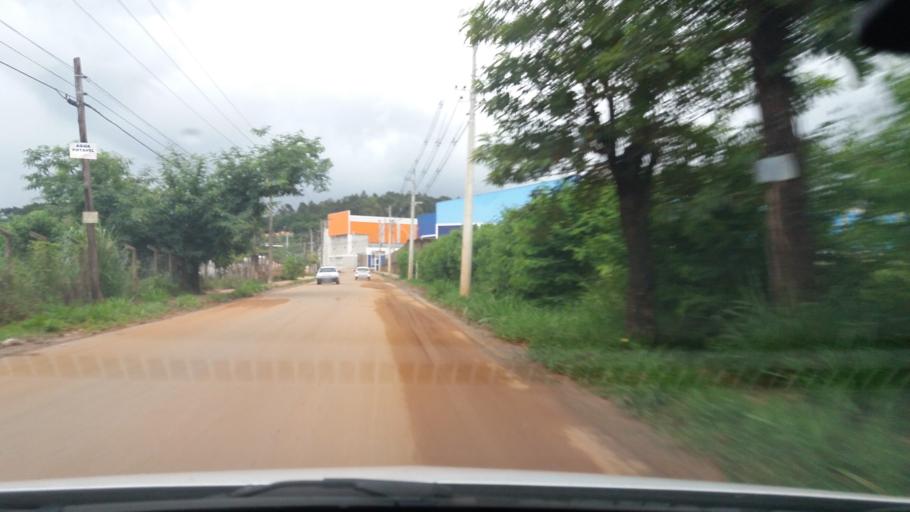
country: BR
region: Sao Paulo
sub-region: Bom Jesus Dos Perdoes
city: Bom Jesus dos Perdoes
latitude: -23.1469
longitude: -46.4594
